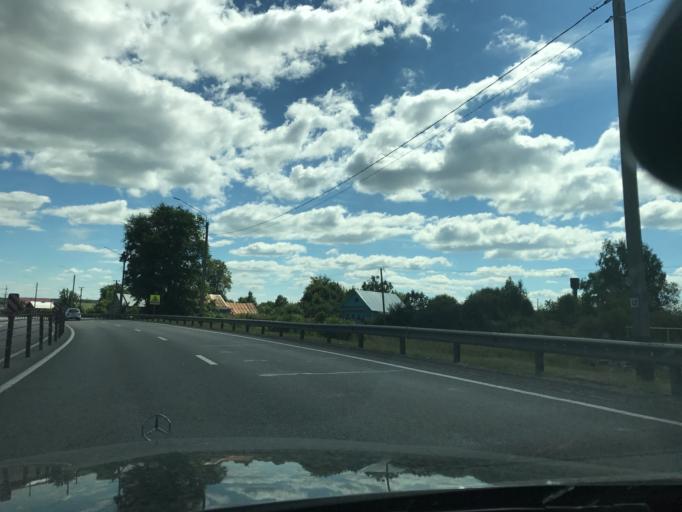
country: RU
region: Vladimir
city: Novovyazniki
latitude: 56.1736
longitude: 42.4178
